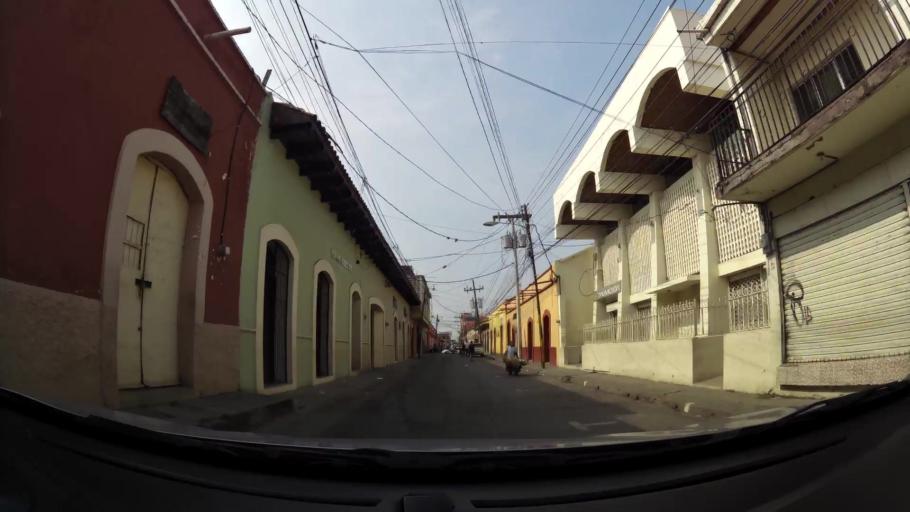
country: HN
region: Comayagua
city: Comayagua
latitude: 14.4588
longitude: -87.6417
